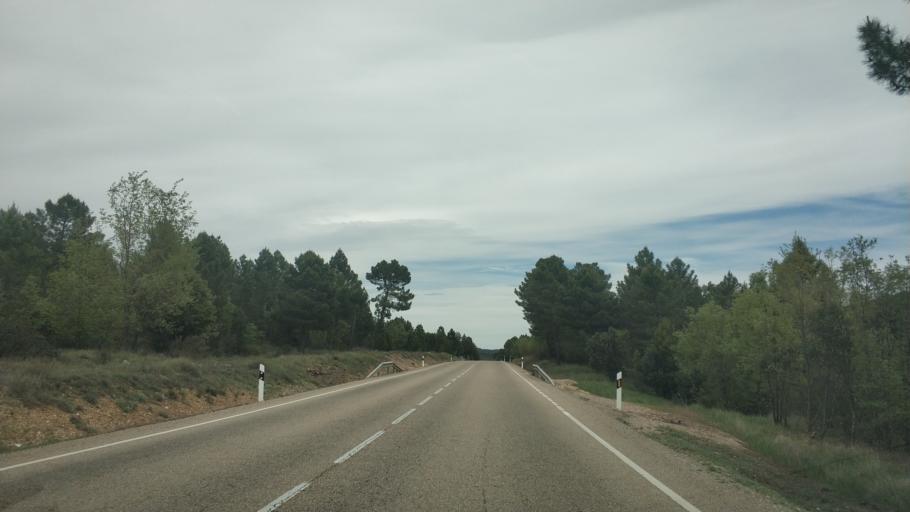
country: ES
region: Castille and Leon
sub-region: Provincia de Soria
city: Bayubas de Abajo
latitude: 41.5104
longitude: -2.9190
